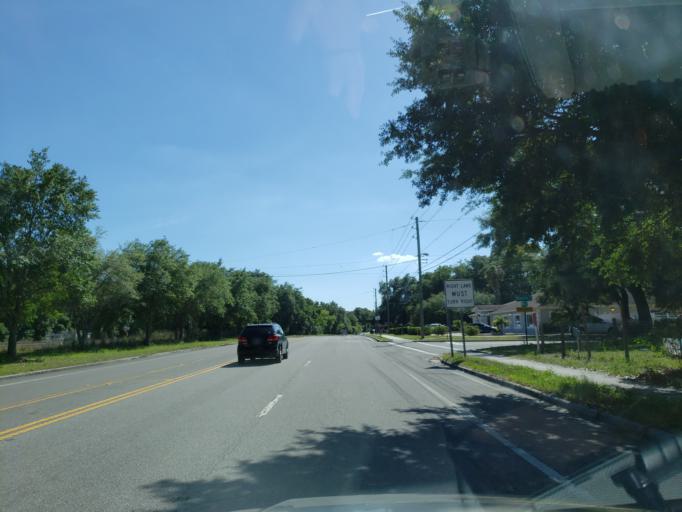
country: US
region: Florida
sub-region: Hillsborough County
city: Mango
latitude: 27.9756
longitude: -82.3129
